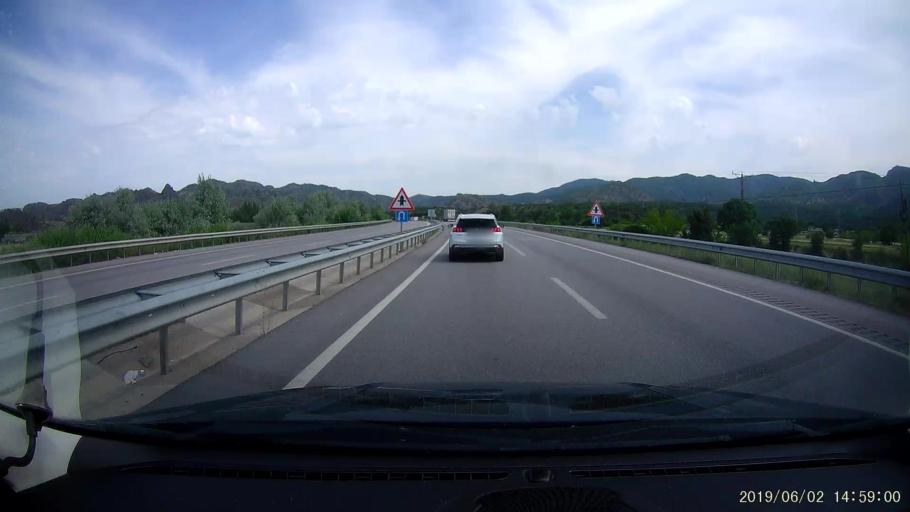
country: TR
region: Corum
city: Osmancik
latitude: 40.9738
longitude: 34.6884
